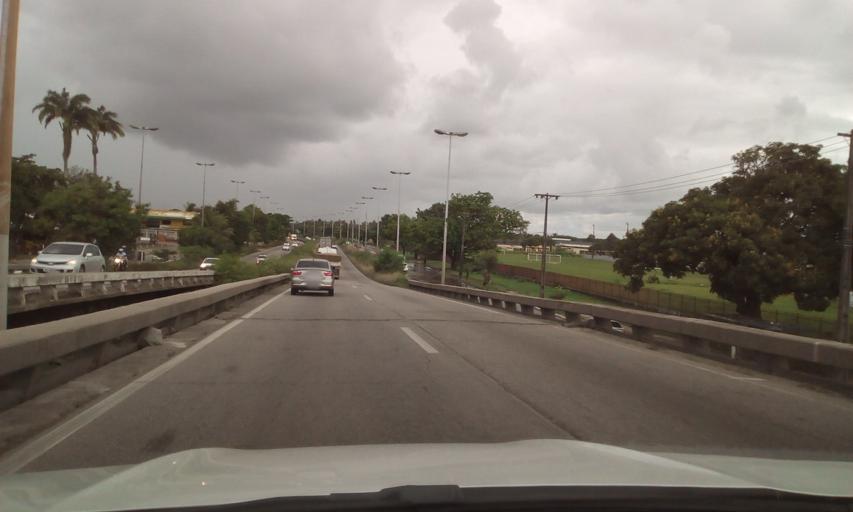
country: BR
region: Pernambuco
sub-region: Recife
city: Recife
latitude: -8.0539
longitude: -34.9465
